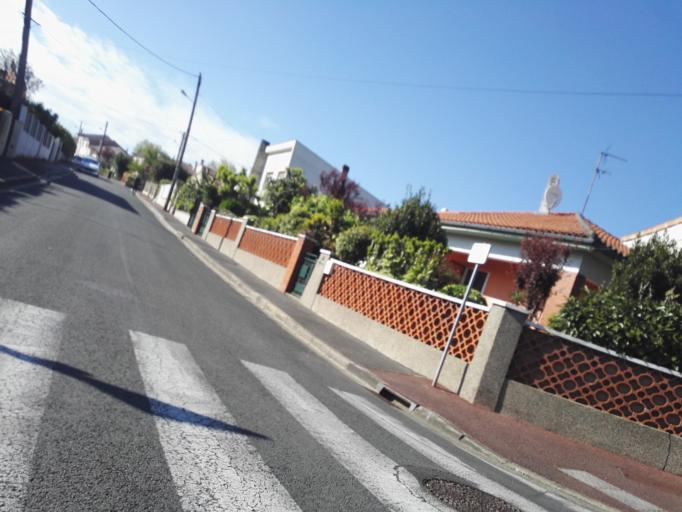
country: FR
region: Aquitaine
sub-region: Departement de la Gironde
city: Talence
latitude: 44.8031
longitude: -0.5827
